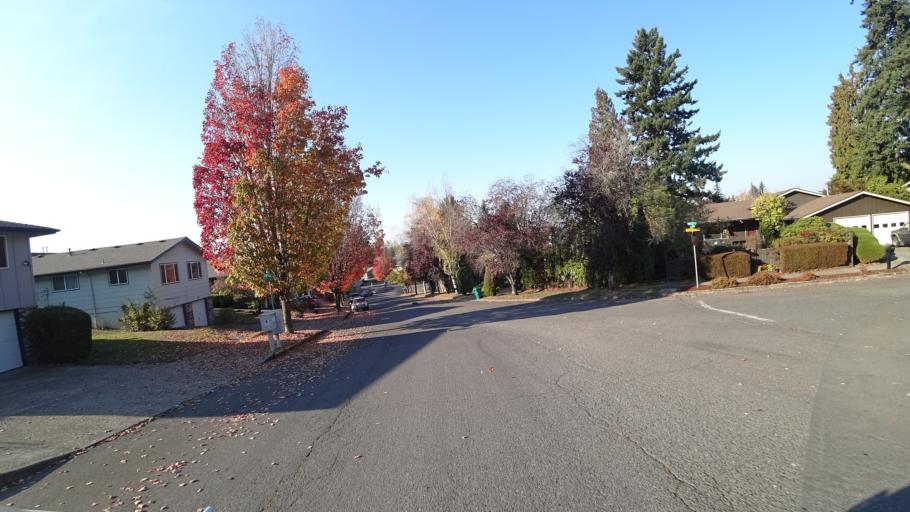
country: US
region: Oregon
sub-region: Multnomah County
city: Gresham
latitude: 45.5061
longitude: -122.4526
